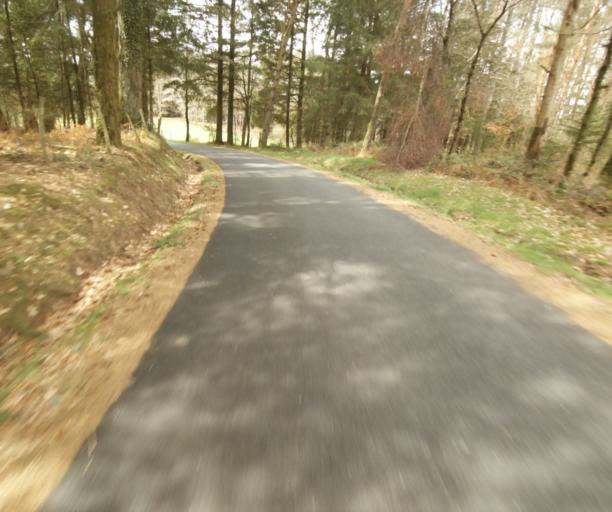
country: FR
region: Limousin
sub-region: Departement de la Correze
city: Correze
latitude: 45.3418
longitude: 1.9584
